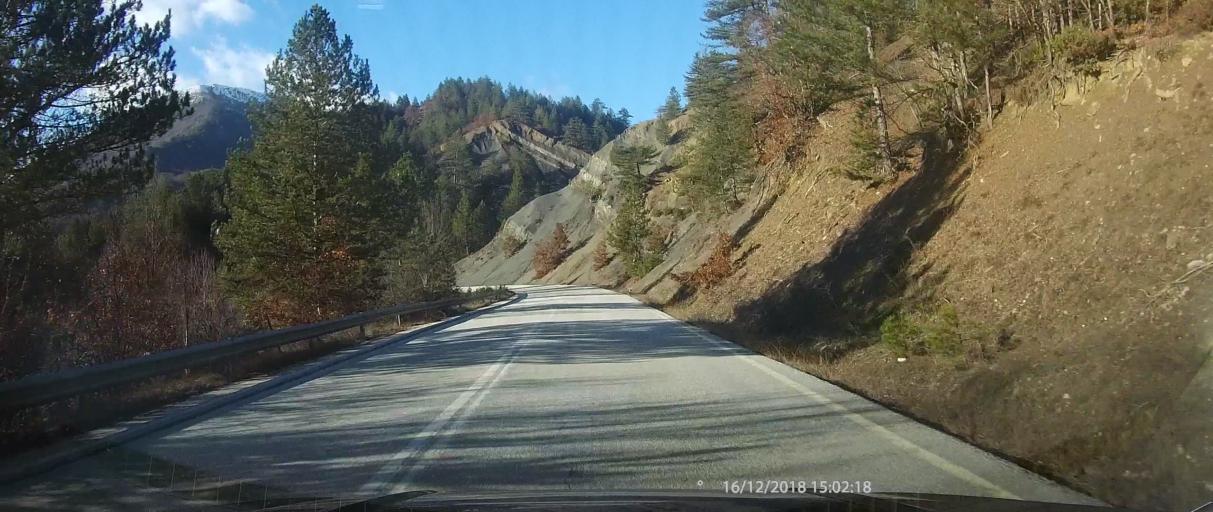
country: GR
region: West Macedonia
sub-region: Nomos Kastorias
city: Nestorio
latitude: 40.2289
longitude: 20.9967
